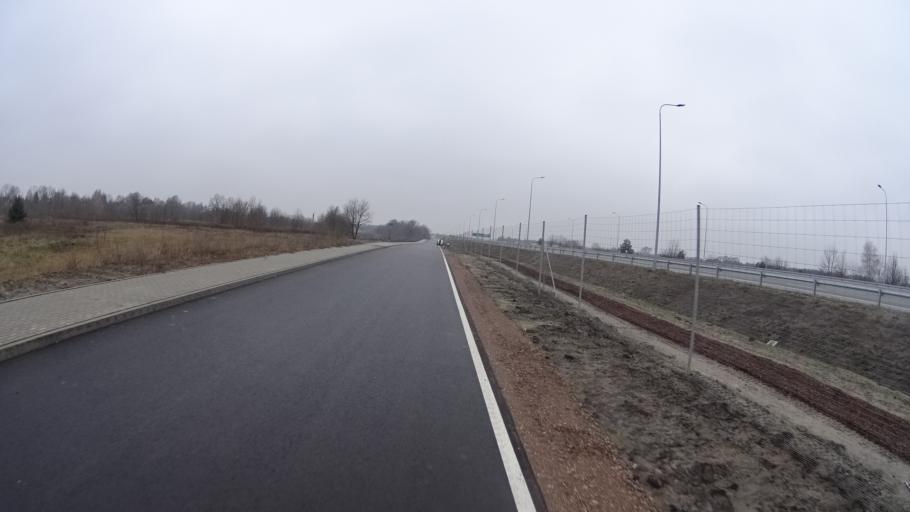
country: PL
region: Masovian Voivodeship
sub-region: Warszawa
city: Wawer
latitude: 52.1651
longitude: 21.1803
